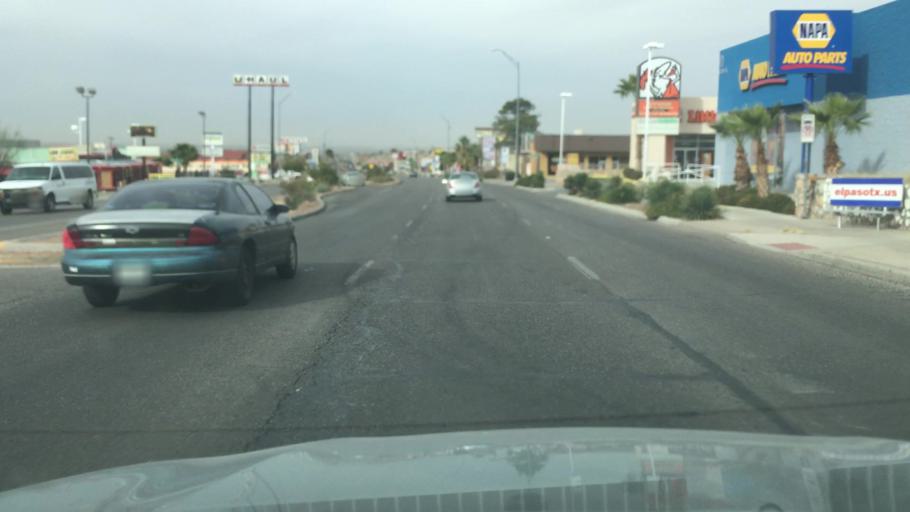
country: US
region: New Mexico
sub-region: Dona Ana County
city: Sunland Park
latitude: 31.8322
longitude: -106.5337
